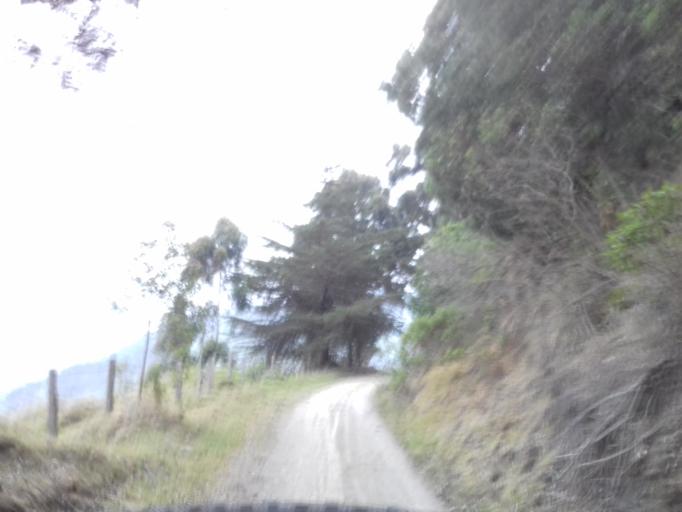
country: CO
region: Tolima
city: Cajamarca
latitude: 4.5282
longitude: -75.4528
